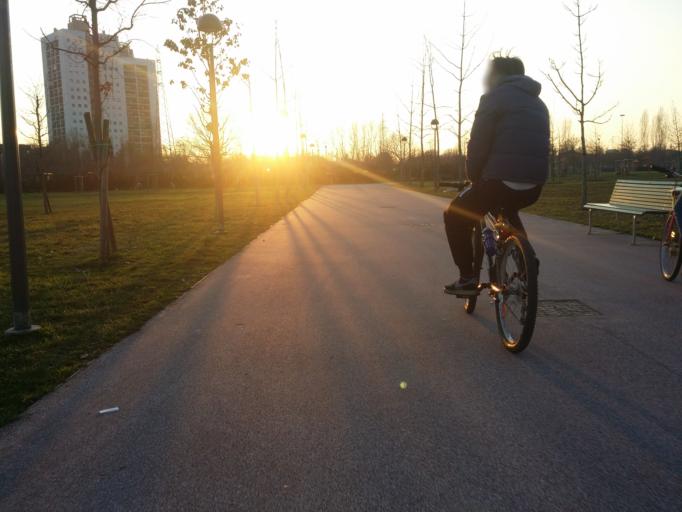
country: IT
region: Lombardy
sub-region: Citta metropolitana di Milano
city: Cesano Boscone
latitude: 45.4498
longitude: 9.1024
